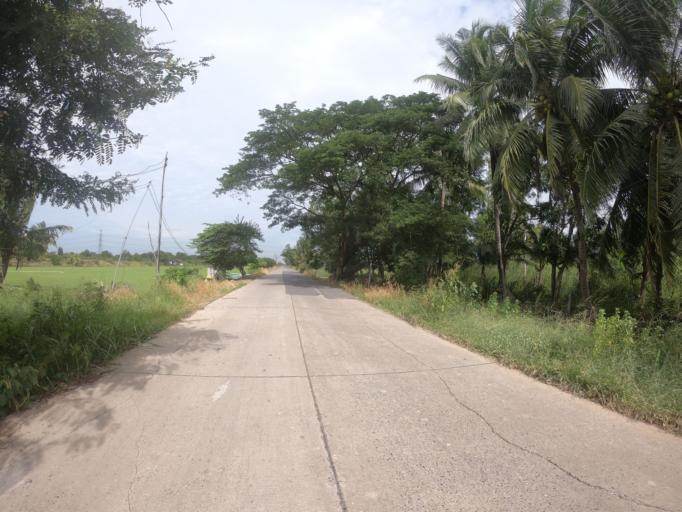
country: TH
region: Pathum Thani
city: Nong Suea
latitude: 14.0319
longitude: 100.8869
